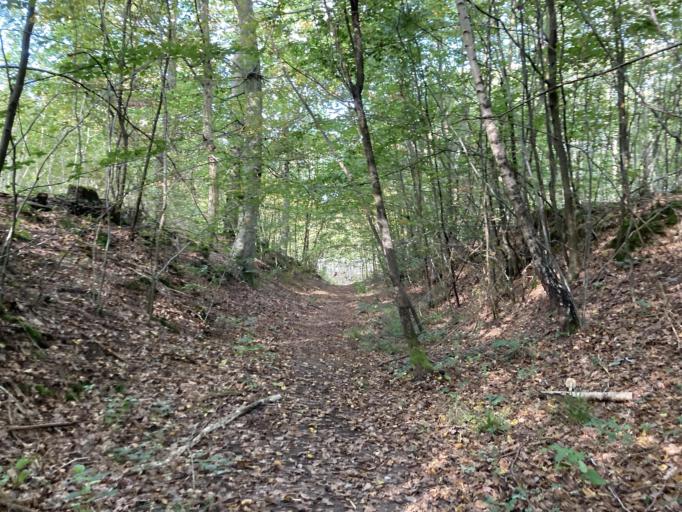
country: FR
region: Ile-de-France
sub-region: Departement des Yvelines
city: Le Pecq
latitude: 48.9151
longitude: 2.1015
